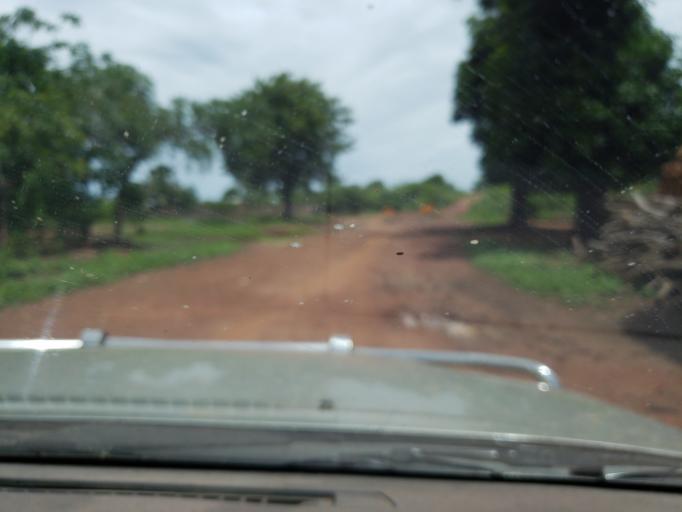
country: ML
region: Sikasso
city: Sikasso
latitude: 11.6750
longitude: -6.1732
